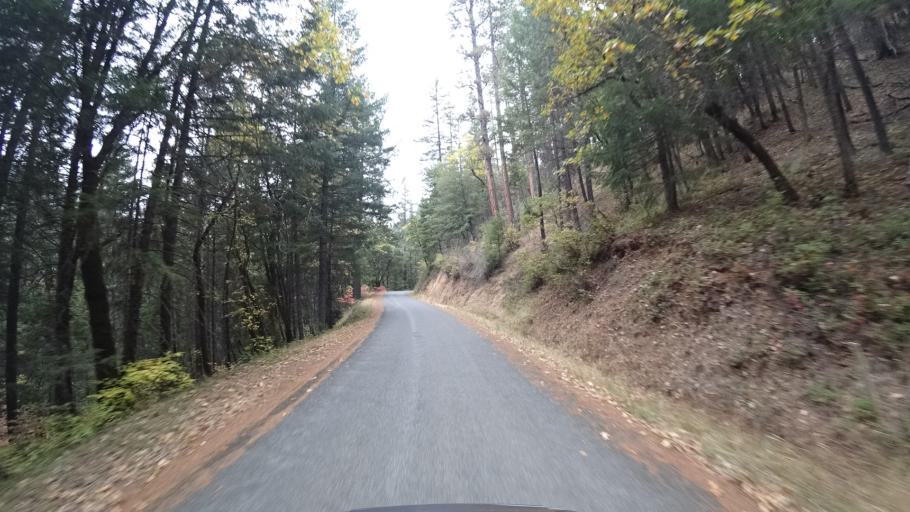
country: US
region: California
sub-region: Siskiyou County
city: Happy Camp
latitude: 41.7629
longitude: -123.3629
